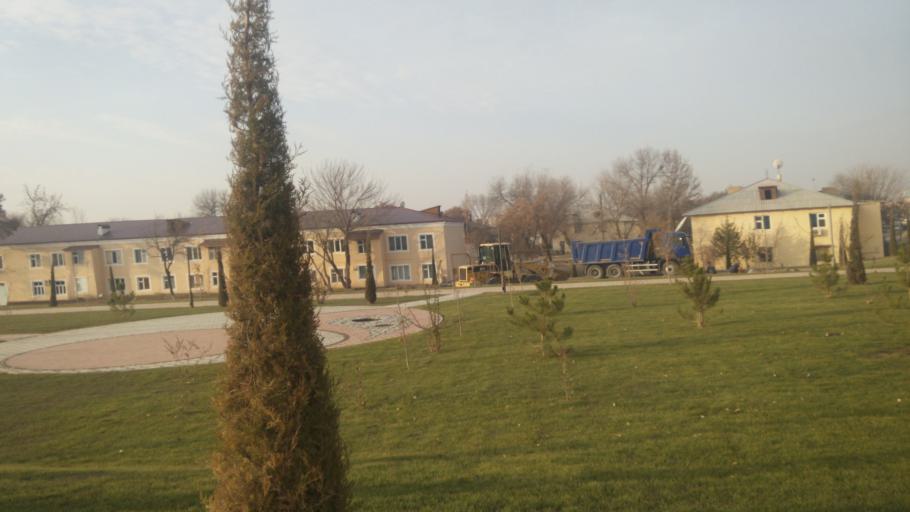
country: UZ
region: Sirdaryo
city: Guliston
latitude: 40.5108
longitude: 68.7771
